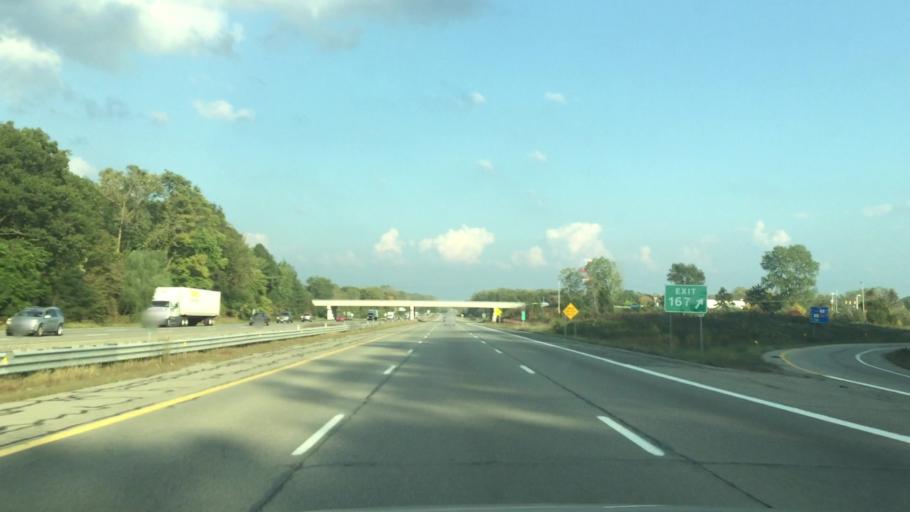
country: US
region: Michigan
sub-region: Washtenaw County
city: Dexter
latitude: 42.2982
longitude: -83.8822
